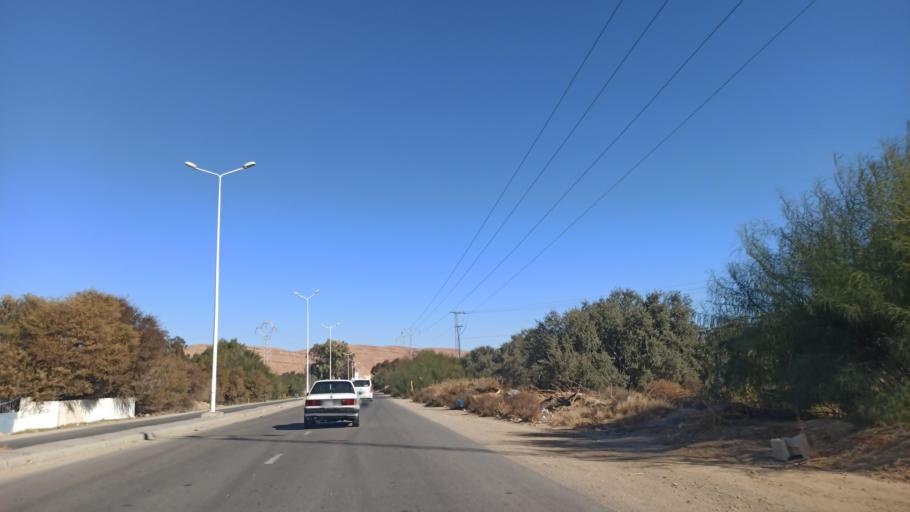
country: TN
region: Gafsa
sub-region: Gafsa Municipality
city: Gafsa
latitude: 34.4174
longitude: 8.7431
